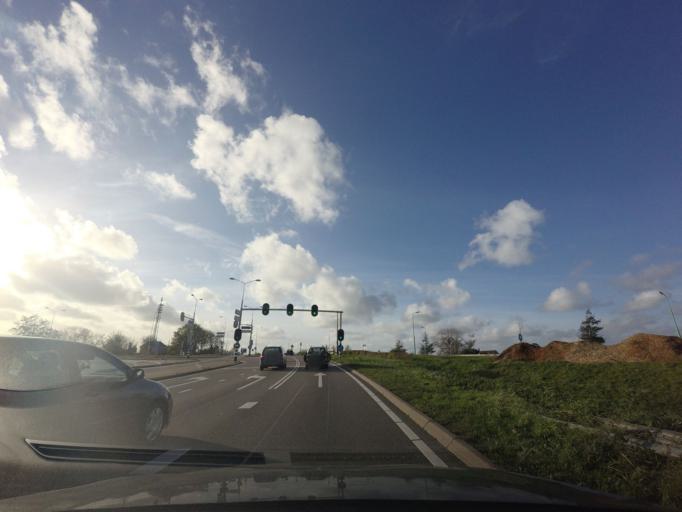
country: NL
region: North Holland
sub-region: Gemeente Langedijk
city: Broek op Langedijk
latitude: 52.7097
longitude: 4.8219
